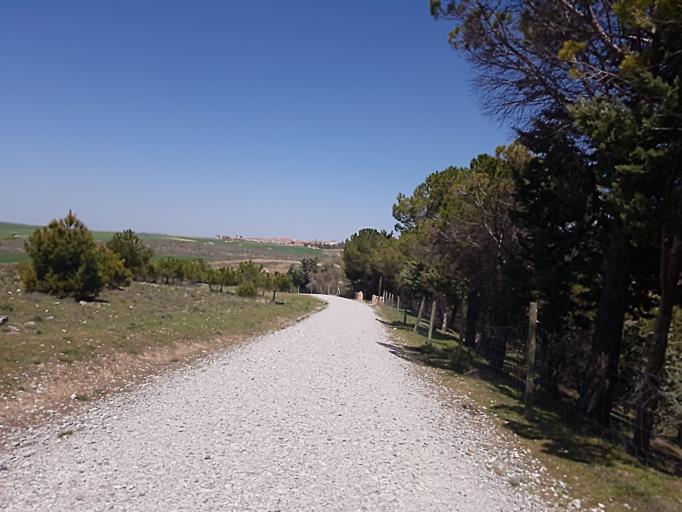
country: ES
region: Castille and Leon
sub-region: Provincia de Segovia
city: Segovia
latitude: 40.9509
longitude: -4.1345
